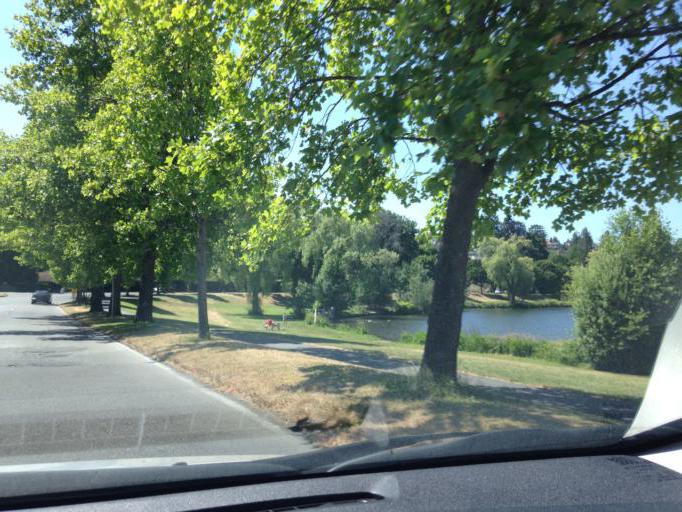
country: US
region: Washington
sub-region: King County
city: Mercer Island
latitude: 47.5700
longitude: -122.2779
